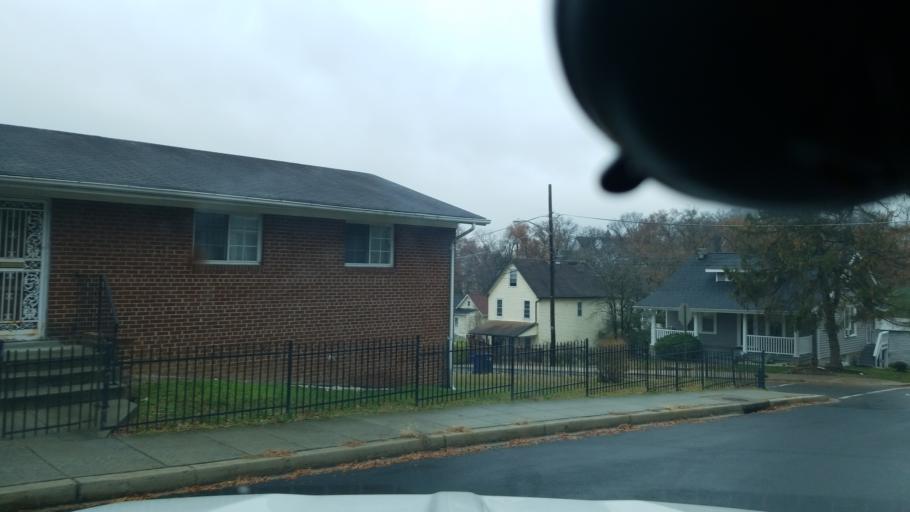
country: US
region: Maryland
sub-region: Prince George's County
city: Mount Rainier
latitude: 38.9276
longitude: -76.9722
